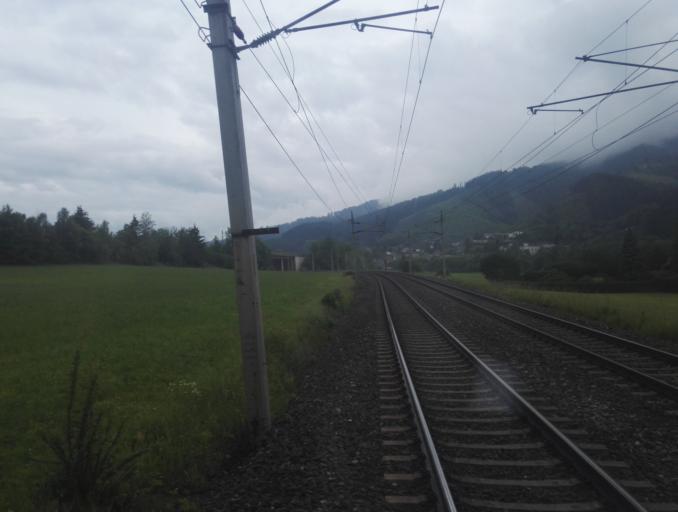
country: AT
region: Styria
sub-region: Politischer Bezirk Bruck-Muerzzuschlag
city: Kindberg
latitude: 47.5116
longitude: 15.4638
